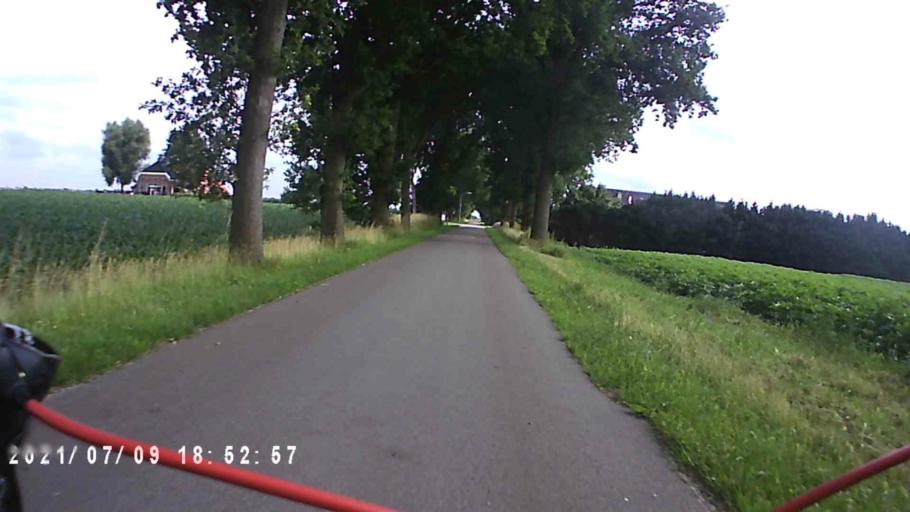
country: NL
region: Groningen
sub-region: Gemeente Stadskanaal
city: Stadskanaal
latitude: 53.0481
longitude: 6.9188
